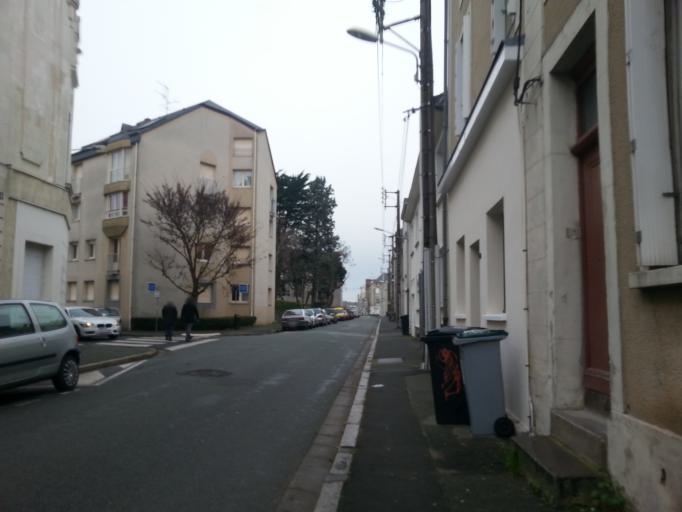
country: FR
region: Pays de la Loire
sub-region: Departement de Maine-et-Loire
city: Angers
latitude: 47.4604
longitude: -0.5586
